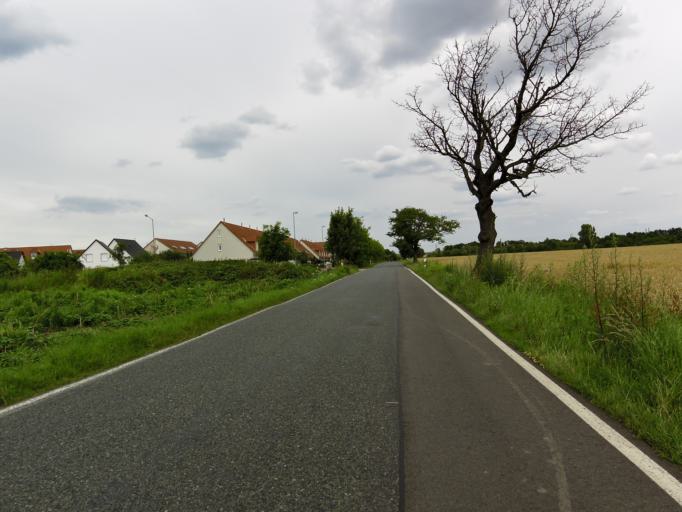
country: DE
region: Saxony
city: Rackwitz
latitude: 51.4036
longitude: 12.3747
